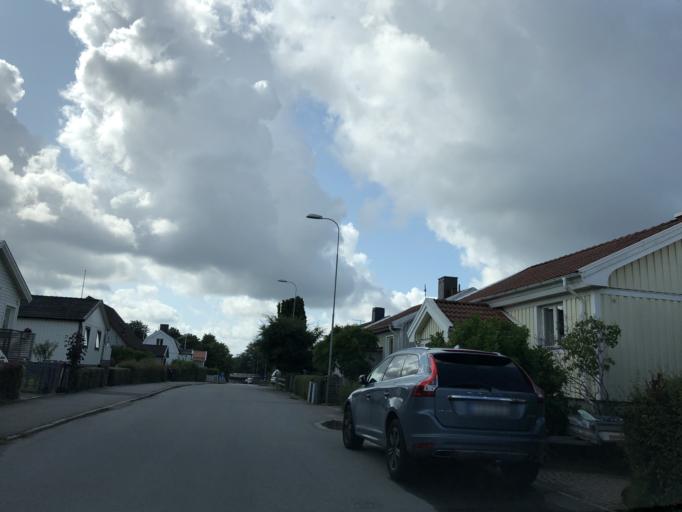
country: SE
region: Vaestra Goetaland
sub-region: Goteborg
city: Majorna
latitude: 57.7160
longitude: 11.9024
